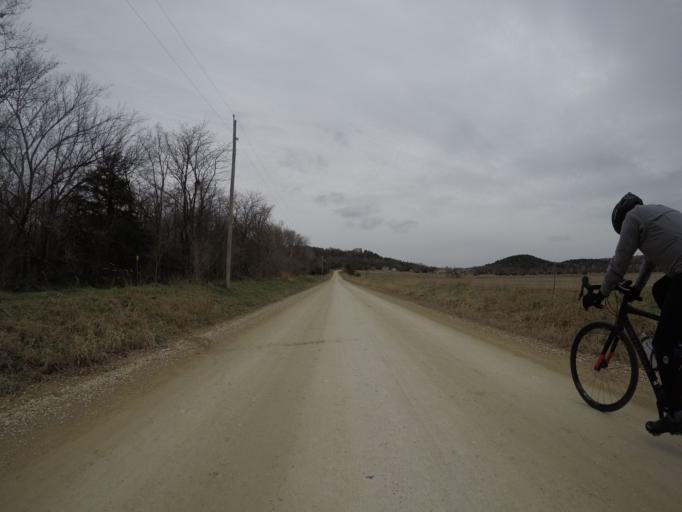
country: US
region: Kansas
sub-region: Riley County
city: Ogden
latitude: 39.1663
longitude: -96.6819
